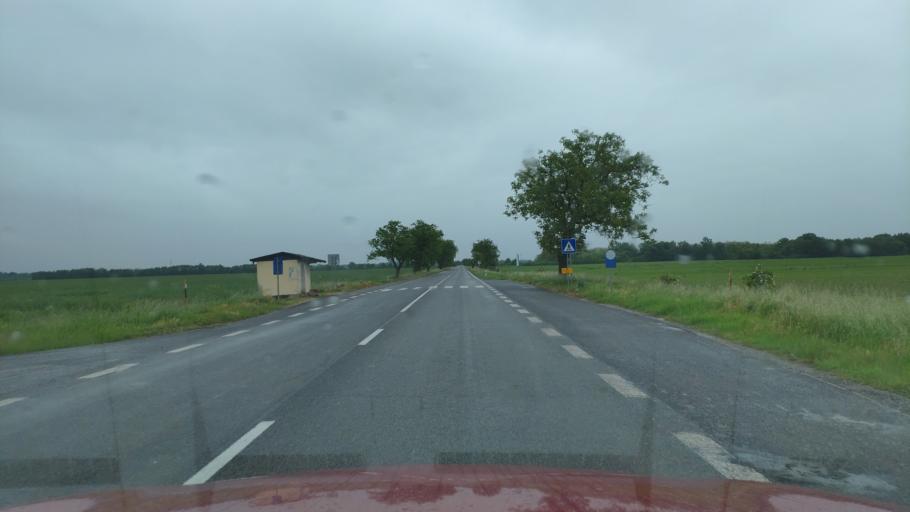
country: HU
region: Borsod-Abauj-Zemplen
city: Karcsa
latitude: 48.4132
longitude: 21.8259
